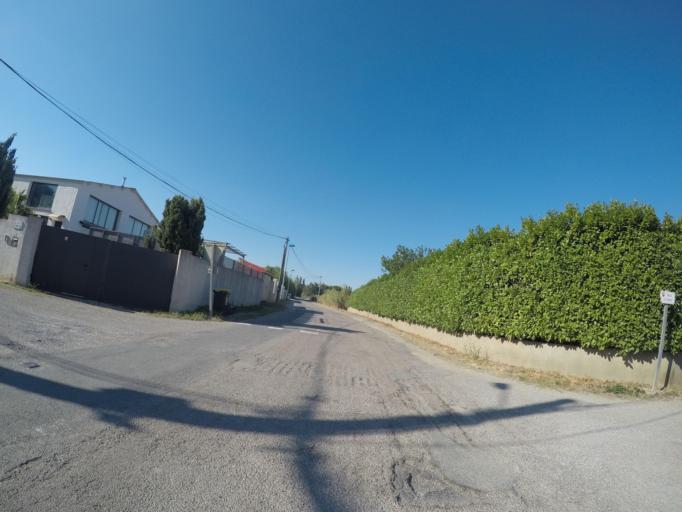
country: FR
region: Languedoc-Roussillon
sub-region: Departement des Pyrenees-Orientales
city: Pezilla-la-Riviere
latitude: 42.6772
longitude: 2.7642
